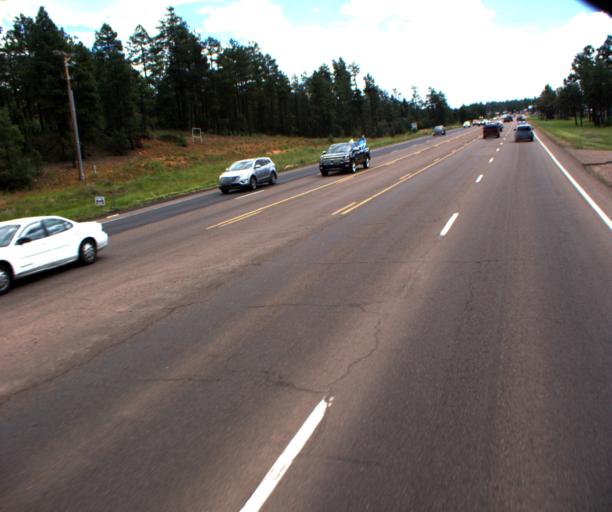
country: US
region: Arizona
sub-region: Navajo County
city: Lake of the Woods
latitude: 34.1756
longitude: -110.0078
